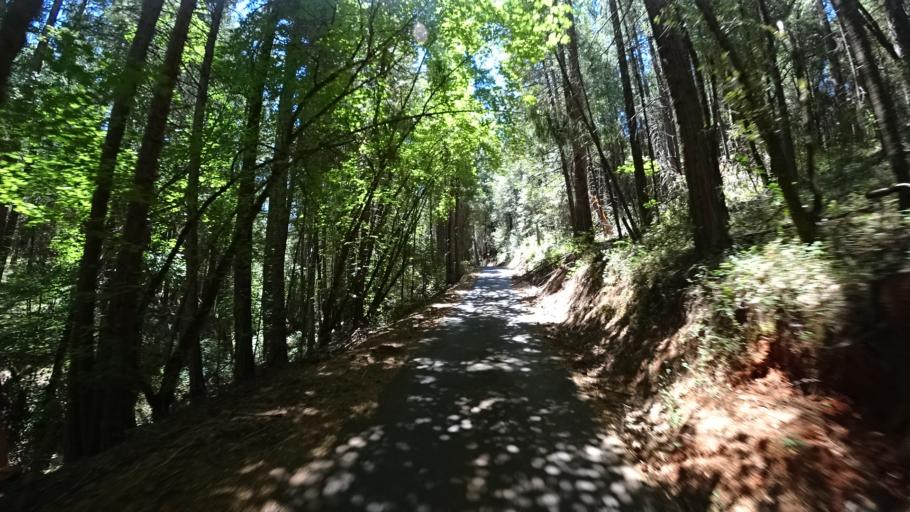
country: US
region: California
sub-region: Amador County
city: Pioneer
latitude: 38.3572
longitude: -120.5600
